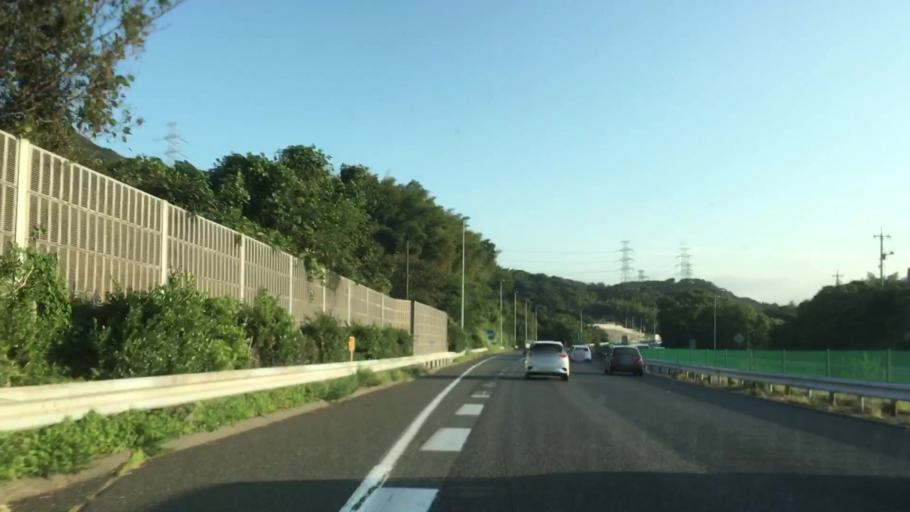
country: JP
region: Yamaguchi
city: Shimonoseki
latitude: 33.9808
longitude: 130.9525
